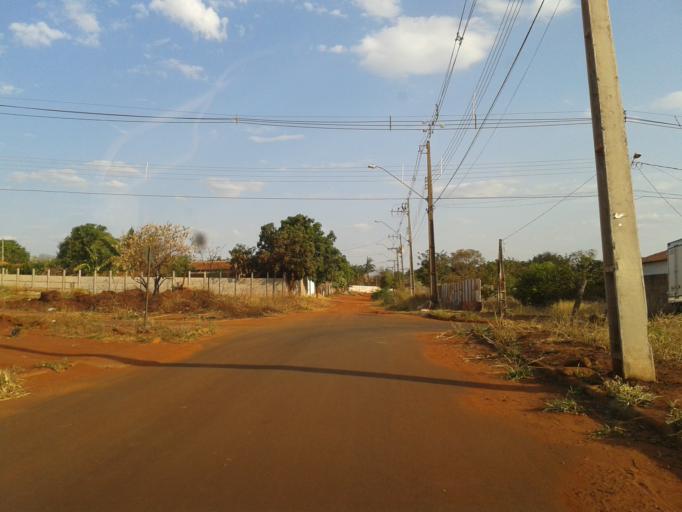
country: BR
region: Minas Gerais
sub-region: Ituiutaba
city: Ituiutaba
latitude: -18.9953
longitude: -49.4367
